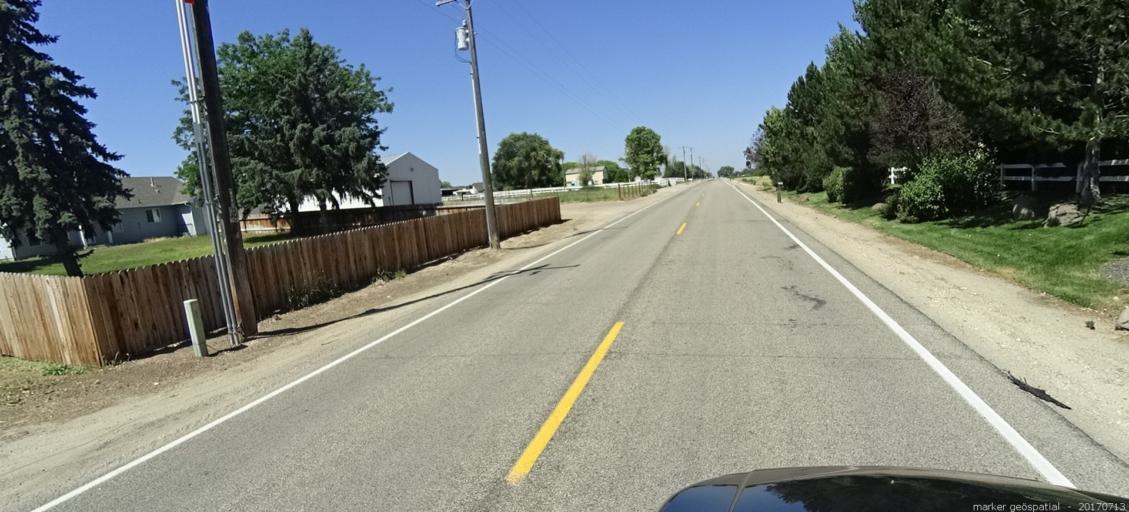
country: US
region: Idaho
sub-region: Ada County
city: Kuna
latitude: 43.5321
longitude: -116.4225
